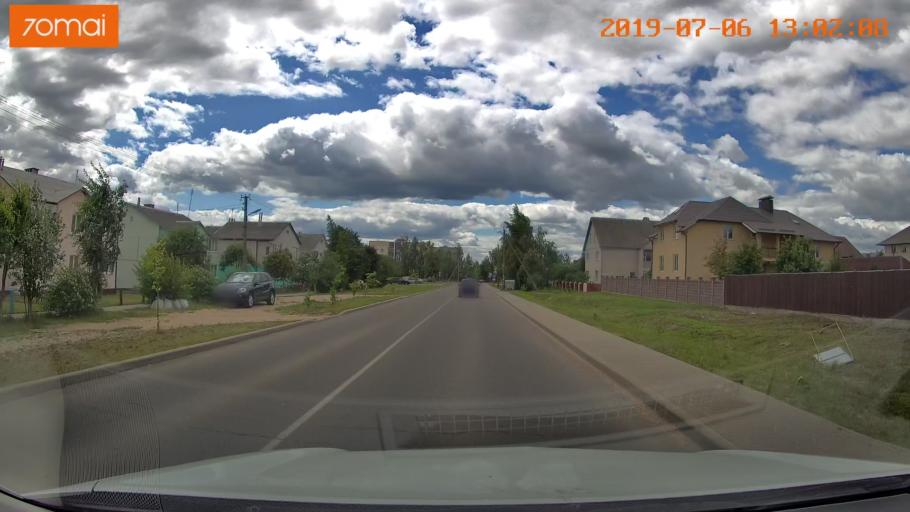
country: BY
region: Minsk
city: Dzyarzhynsk
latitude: 53.6876
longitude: 27.1183
